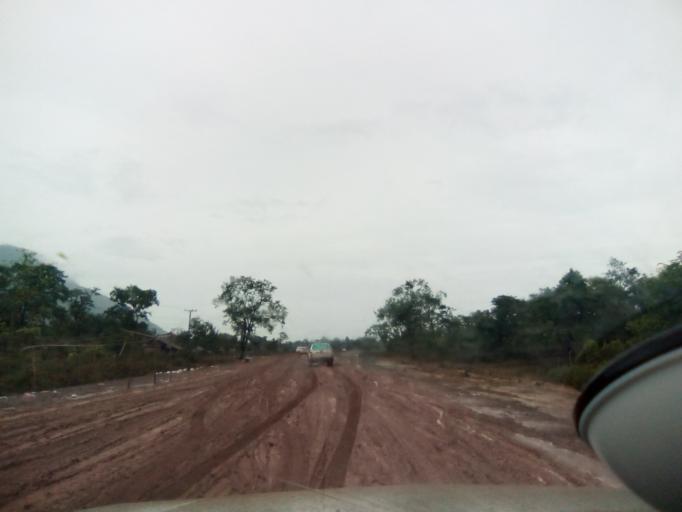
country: LA
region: Attapu
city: Attapu
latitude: 14.6905
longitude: 106.5381
